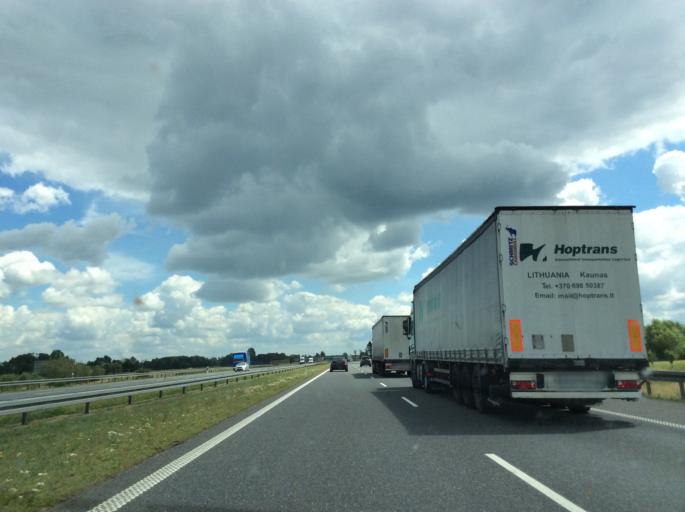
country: PL
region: Greater Poland Voivodeship
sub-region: Powiat kolski
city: Dabie
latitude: 52.0557
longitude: 18.8402
